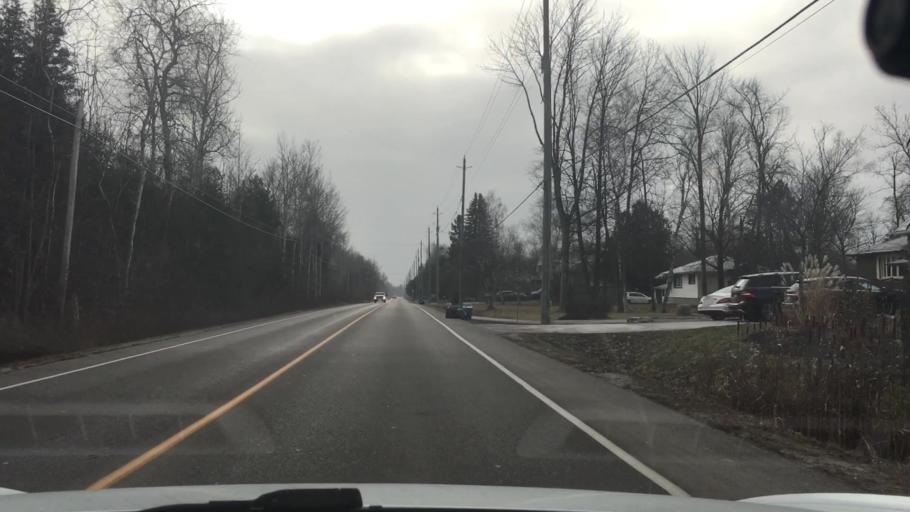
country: CA
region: Ontario
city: Oshawa
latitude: 43.9278
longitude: -78.7960
